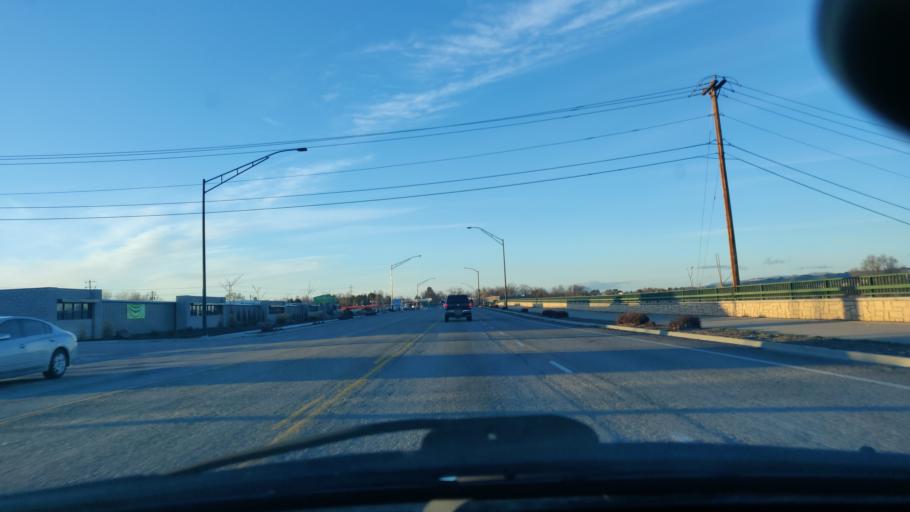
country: US
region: Idaho
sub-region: Ada County
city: Boise
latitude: 43.5761
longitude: -116.1948
